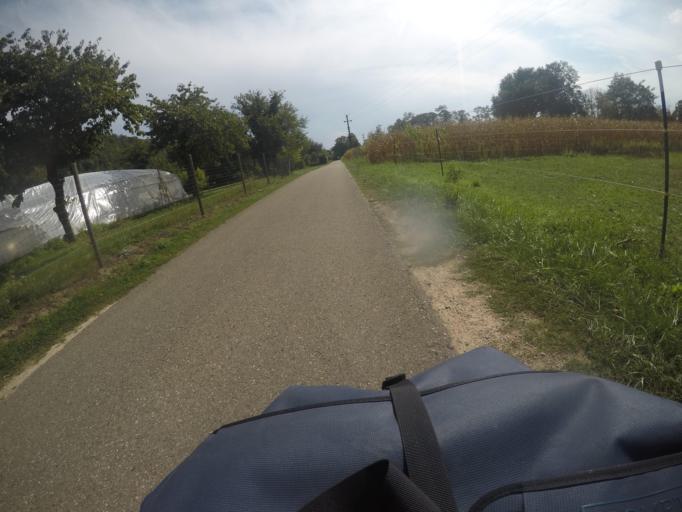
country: FR
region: Alsace
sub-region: Departement du Haut-Rhin
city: Kembs
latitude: 47.6933
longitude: 7.5234
